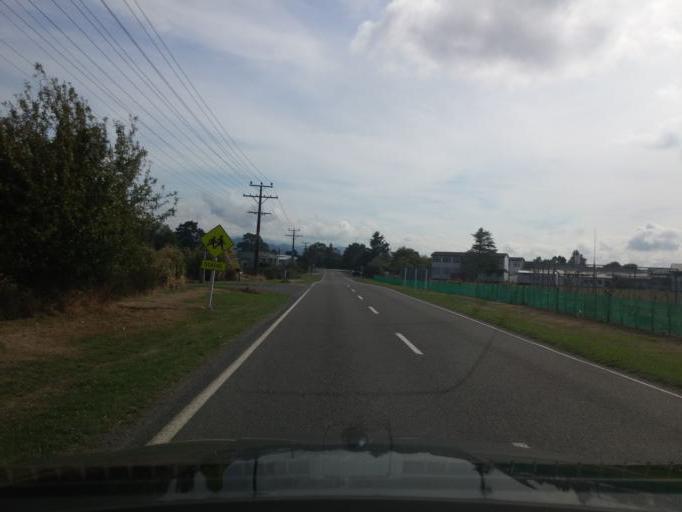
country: NZ
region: Wellington
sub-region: Masterton District
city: Masterton
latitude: -41.0938
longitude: 175.4492
